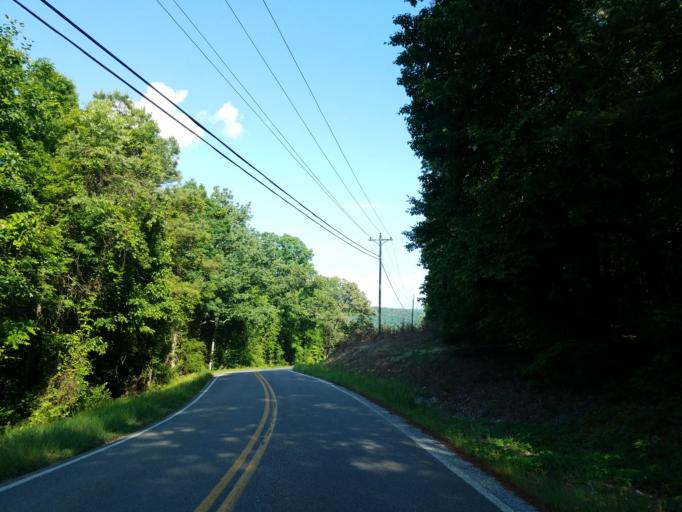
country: US
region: Georgia
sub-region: Pickens County
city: Nelson
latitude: 34.3772
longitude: -84.3581
